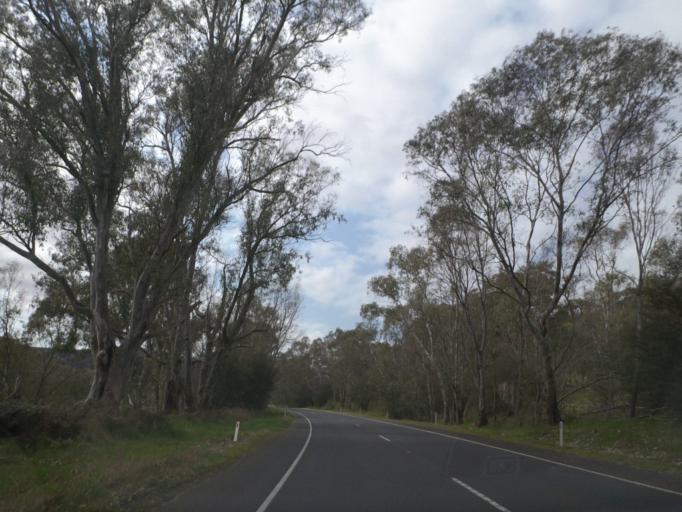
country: AU
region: Victoria
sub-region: Murrindindi
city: Kinglake West
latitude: -37.1447
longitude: 145.2479
